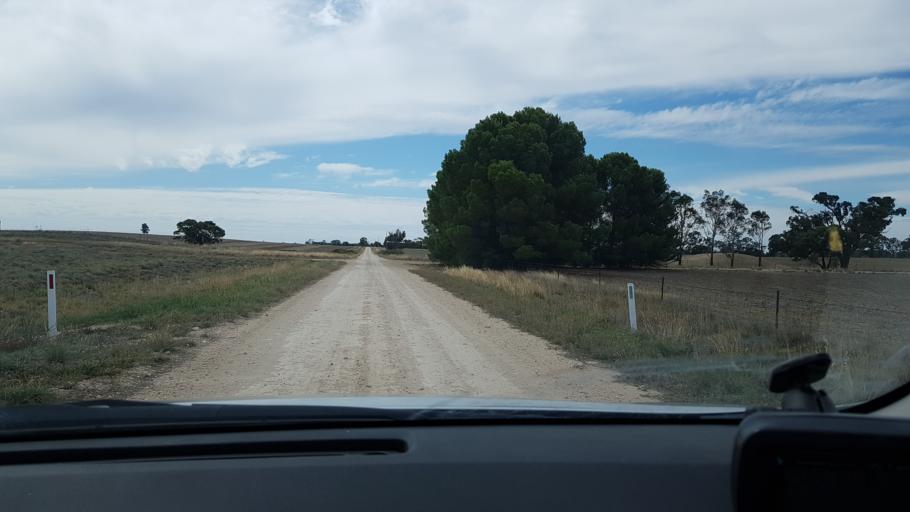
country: AU
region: Victoria
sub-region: Horsham
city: Horsham
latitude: -36.7055
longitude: 141.7806
